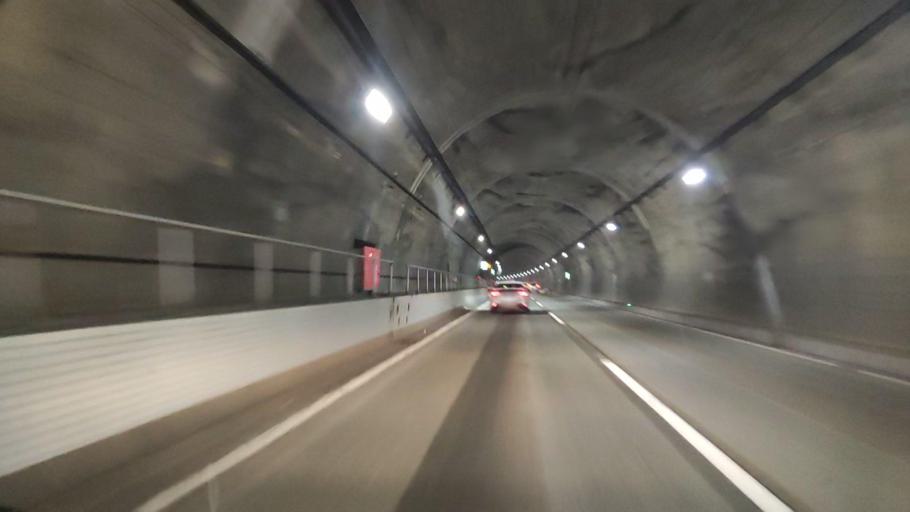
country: JP
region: Iwate
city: Ichinohe
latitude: 40.2334
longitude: 141.3894
